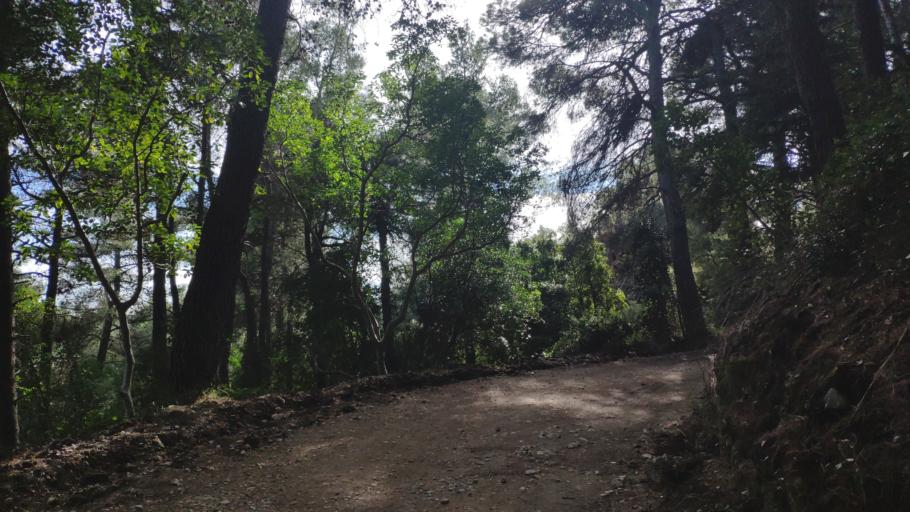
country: GR
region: Attica
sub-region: Nomarchia Anatolikis Attikis
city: Varybobi
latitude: 38.1622
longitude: 23.7771
